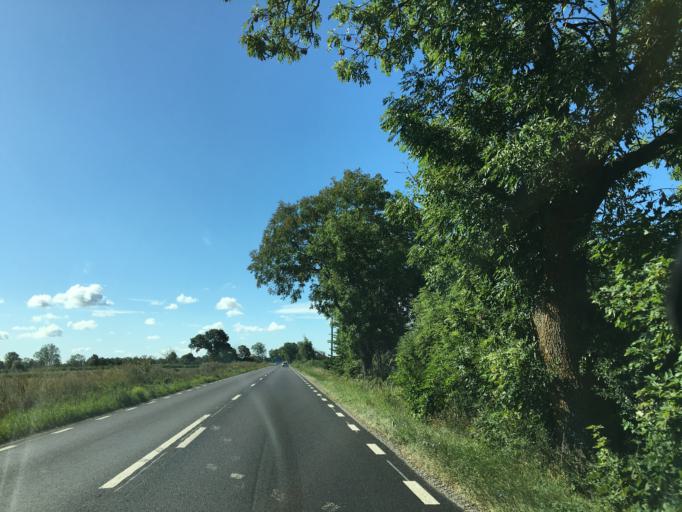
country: SE
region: Kalmar
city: Faerjestaden
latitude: 56.6594
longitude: 16.5180
